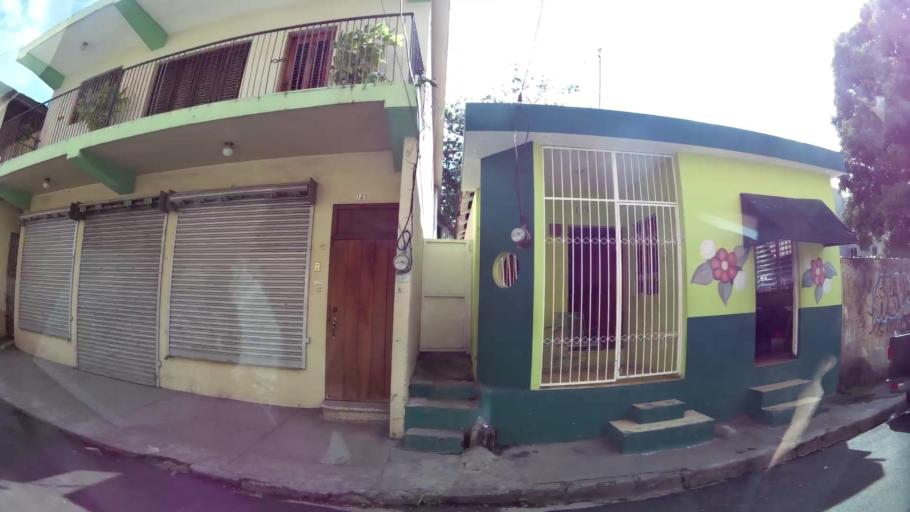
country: DO
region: La Vega
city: Concepcion de La Vega
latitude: 19.2267
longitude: -70.5306
